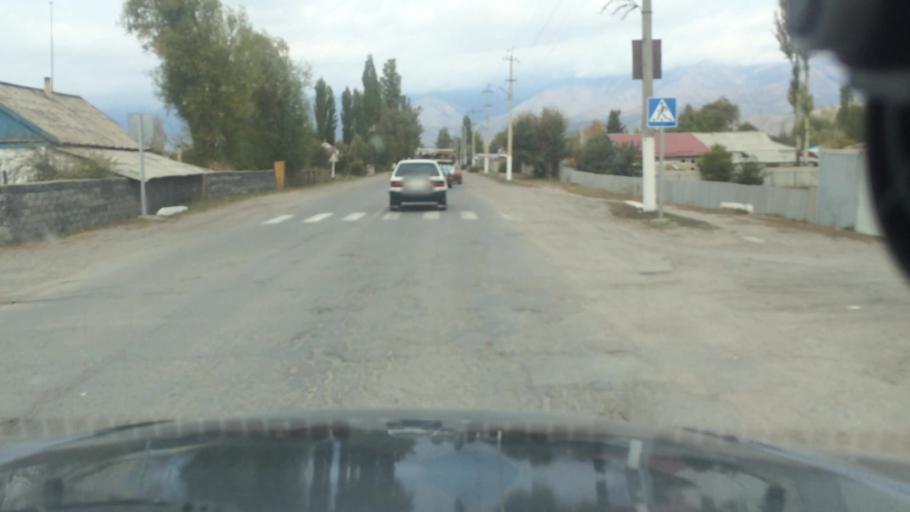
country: KG
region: Ysyk-Koel
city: Tyup
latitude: 42.7239
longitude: 78.3656
